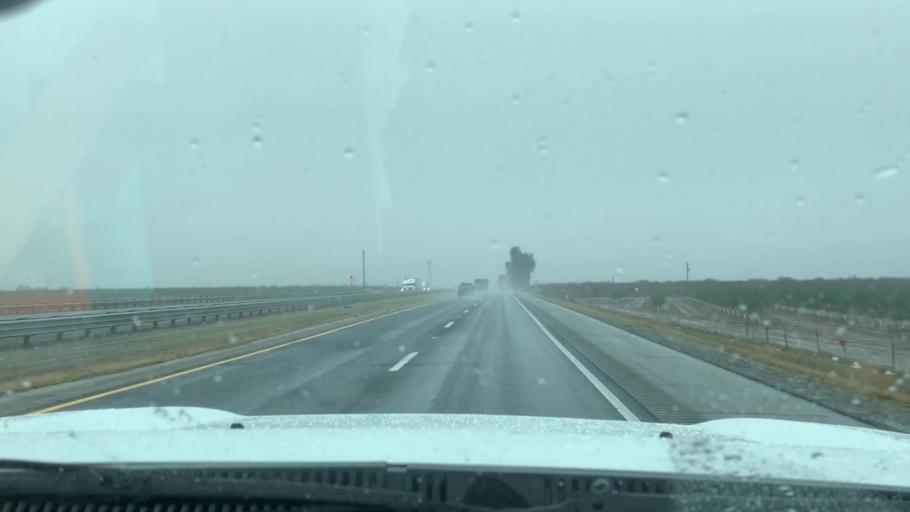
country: US
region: California
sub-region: Tulare County
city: Earlimart
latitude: 35.8530
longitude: -119.2668
